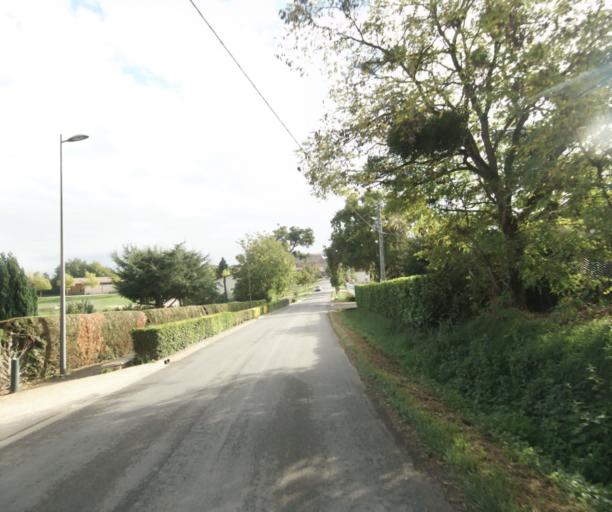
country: FR
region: Midi-Pyrenees
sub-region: Departement du Gers
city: Eauze
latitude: 43.8652
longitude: 0.1011
